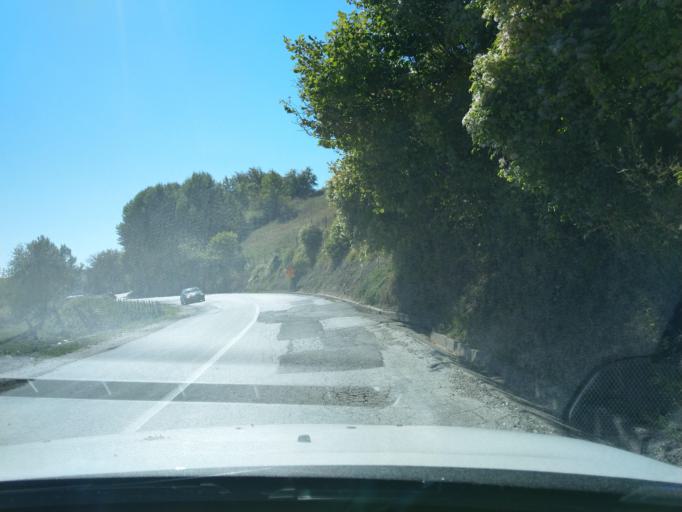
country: RS
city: Sokolovica
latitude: 43.2600
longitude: 20.2325
